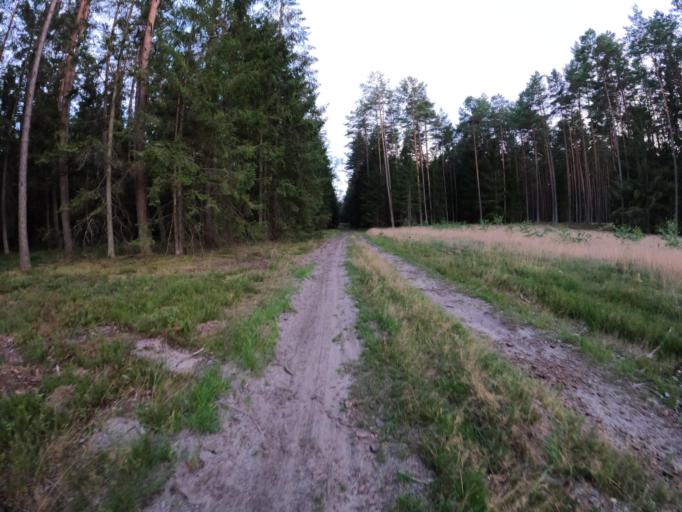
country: PL
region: West Pomeranian Voivodeship
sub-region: Powiat koszalinski
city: Sianow
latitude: 54.0961
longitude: 16.4101
